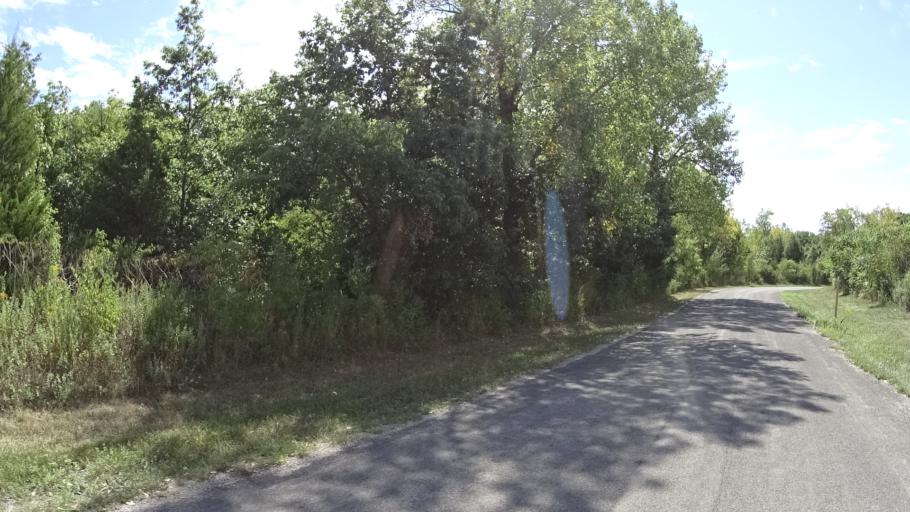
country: US
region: Ohio
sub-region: Erie County
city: Sandusky
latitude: 41.5999
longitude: -82.7216
